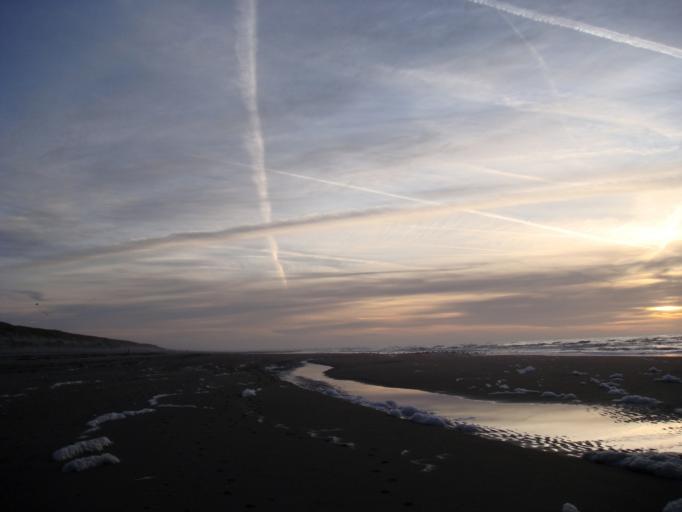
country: NL
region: North Holland
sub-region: Gemeente Texel
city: Den Burg
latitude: 53.0487
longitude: 4.7156
